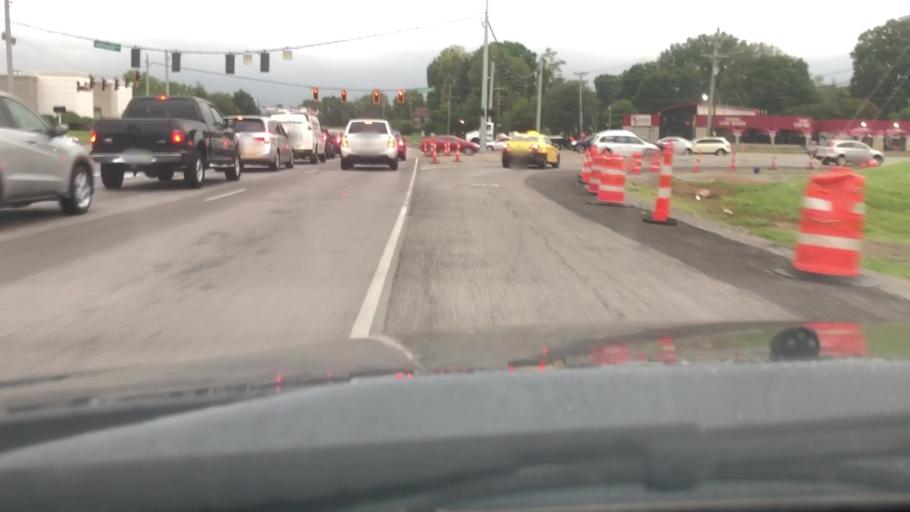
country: US
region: Kentucky
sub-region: Jefferson County
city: Hurstbourne Acres
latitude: 38.2152
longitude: -85.5903
